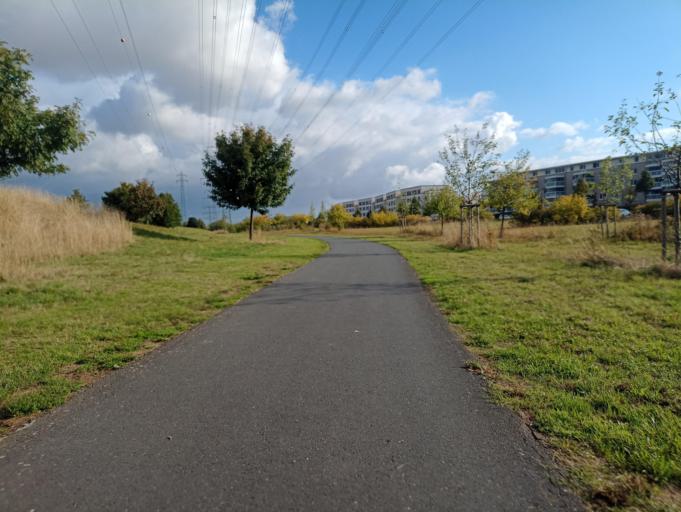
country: DE
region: Hesse
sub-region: Regierungsbezirk Darmstadt
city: Steinbach am Taunus
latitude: 50.1769
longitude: 8.6153
